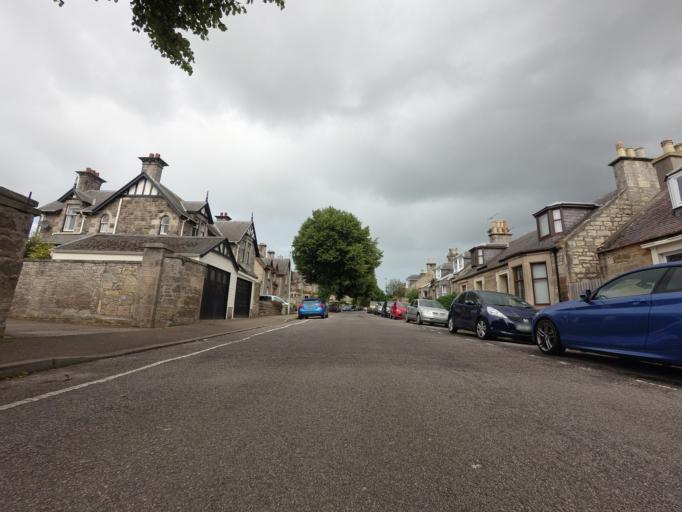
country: GB
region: Scotland
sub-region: Moray
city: Elgin
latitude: 57.6440
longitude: -3.3114
